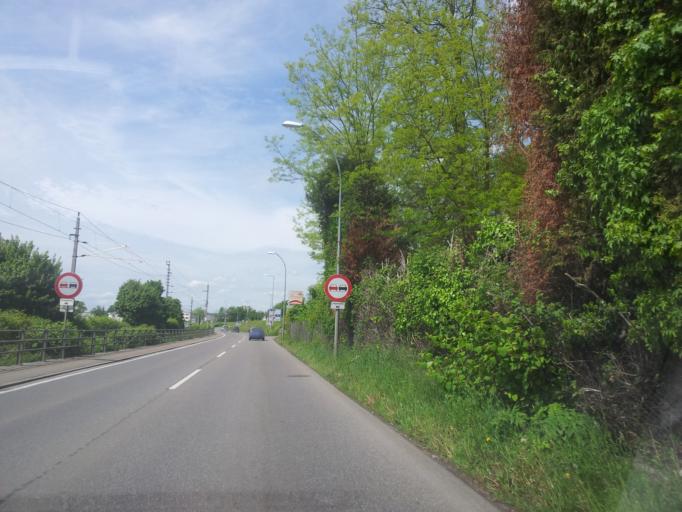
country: AT
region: Vorarlberg
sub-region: Politischer Bezirk Bregenz
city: Lochau
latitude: 47.5201
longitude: 9.7524
